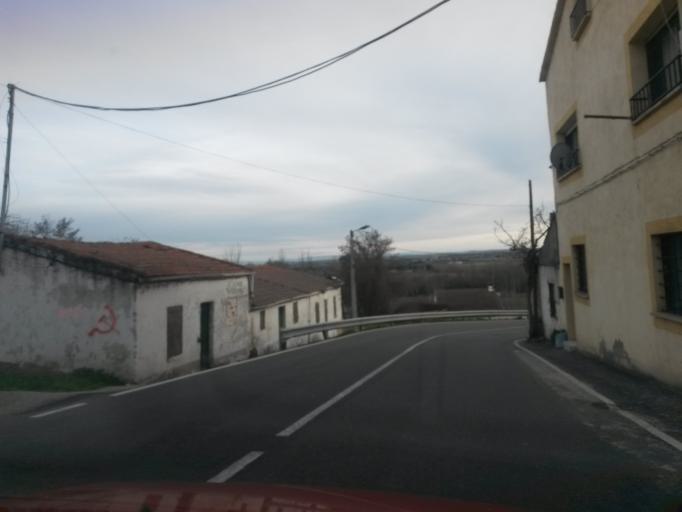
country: ES
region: Castille and Leon
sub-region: Provincia de Salamanca
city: Cabrerizos
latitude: 40.9766
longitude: -5.6101
